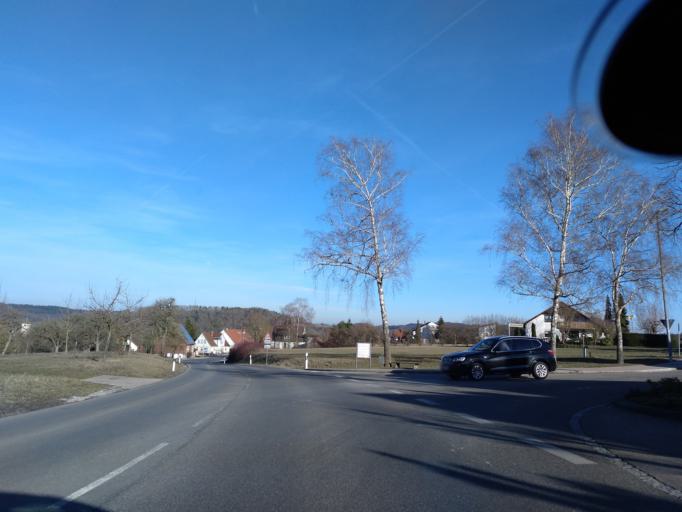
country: DE
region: Baden-Wuerttemberg
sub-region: Regierungsbezirk Stuttgart
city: Vellberg
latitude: 49.0849
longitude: 9.8729
